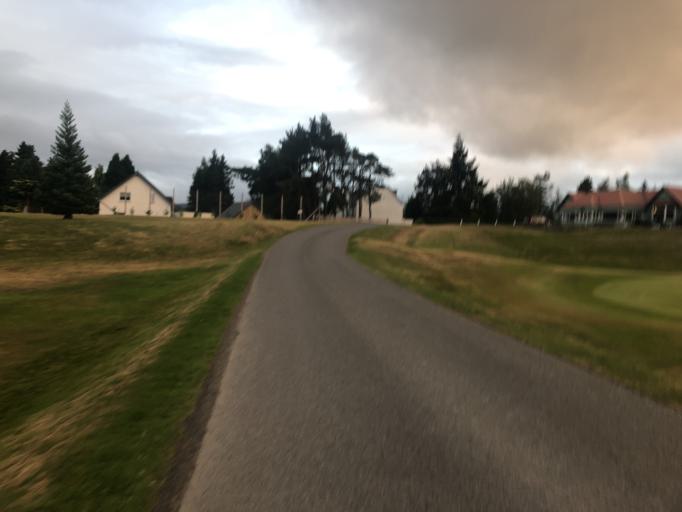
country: GB
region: Scotland
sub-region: Highland
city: Kingussie
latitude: 57.0647
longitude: -4.1178
